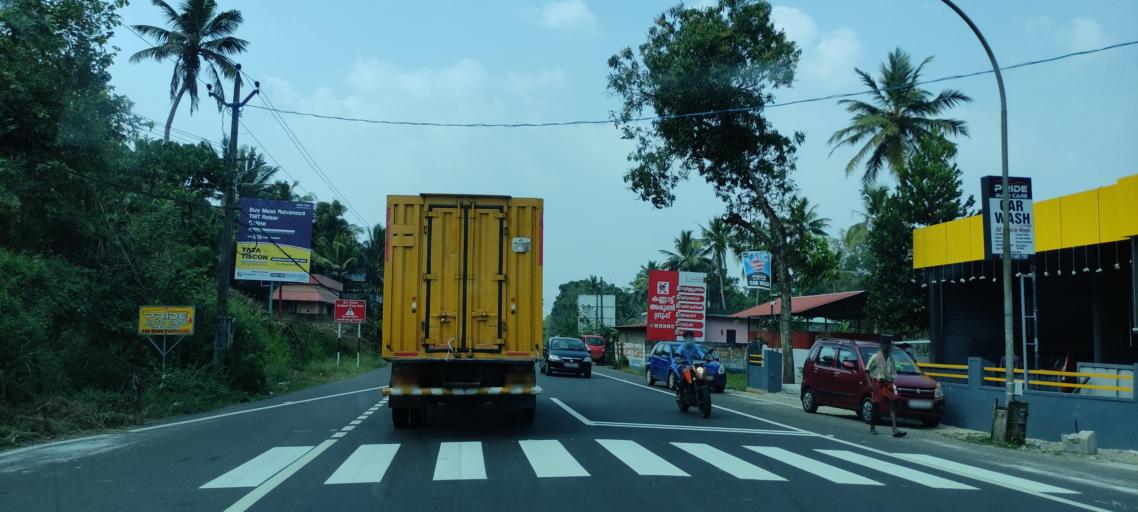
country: IN
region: Kerala
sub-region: Alappuzha
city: Chengannur
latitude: 9.2839
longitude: 76.6539
